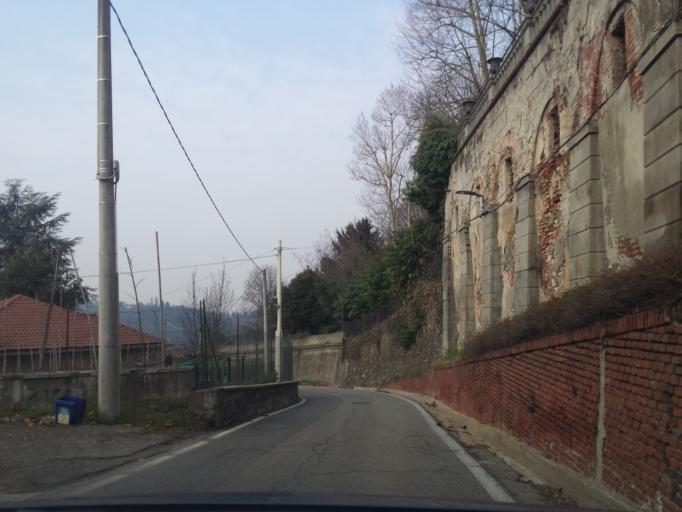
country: IT
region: Piedmont
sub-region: Provincia di Torino
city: Turin
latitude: 45.0562
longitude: 7.7110
